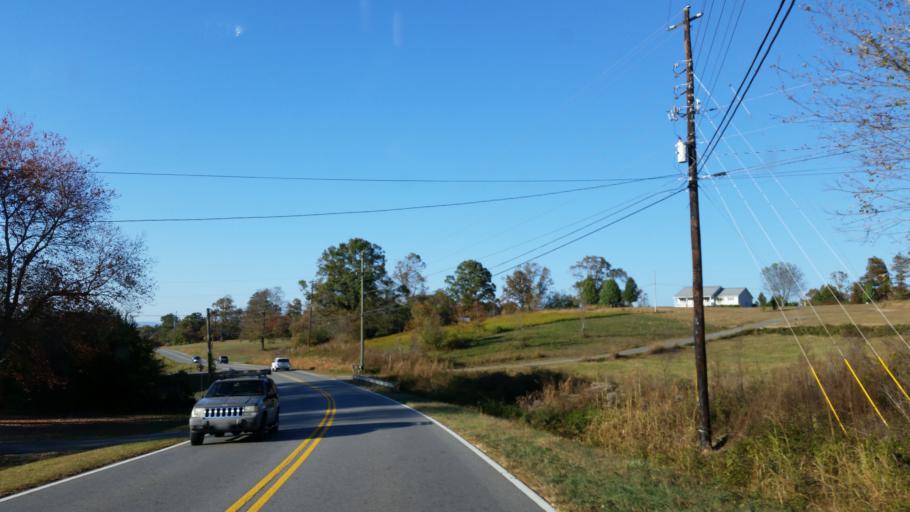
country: US
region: Georgia
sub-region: Gilmer County
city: Ellijay
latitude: 34.6511
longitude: -84.4694
